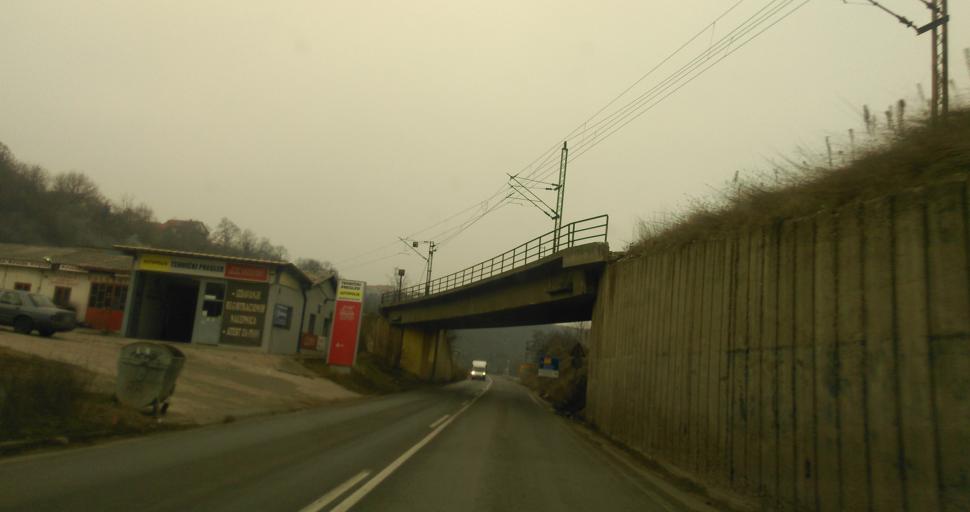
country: RS
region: Central Serbia
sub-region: Belgrade
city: Rakovica
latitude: 44.7226
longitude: 20.4546
